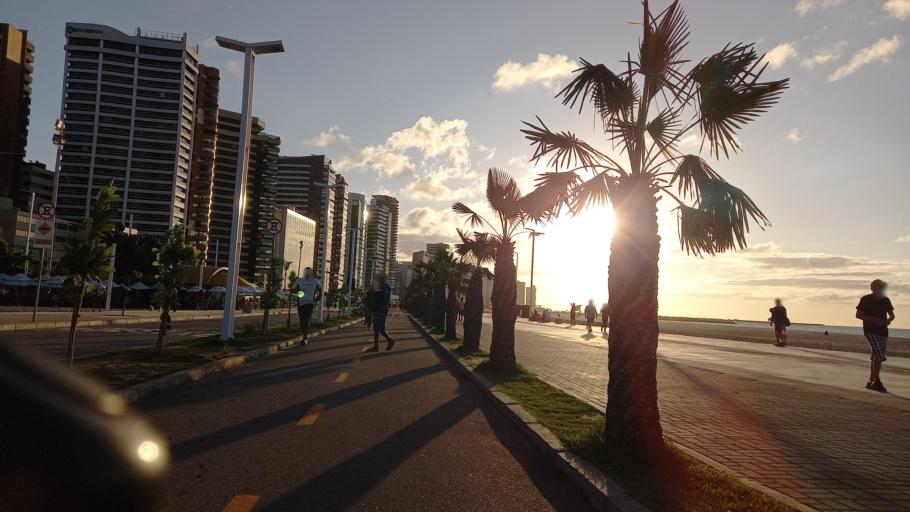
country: BR
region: Ceara
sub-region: Fortaleza
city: Fortaleza
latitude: -3.7248
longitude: -38.4979
